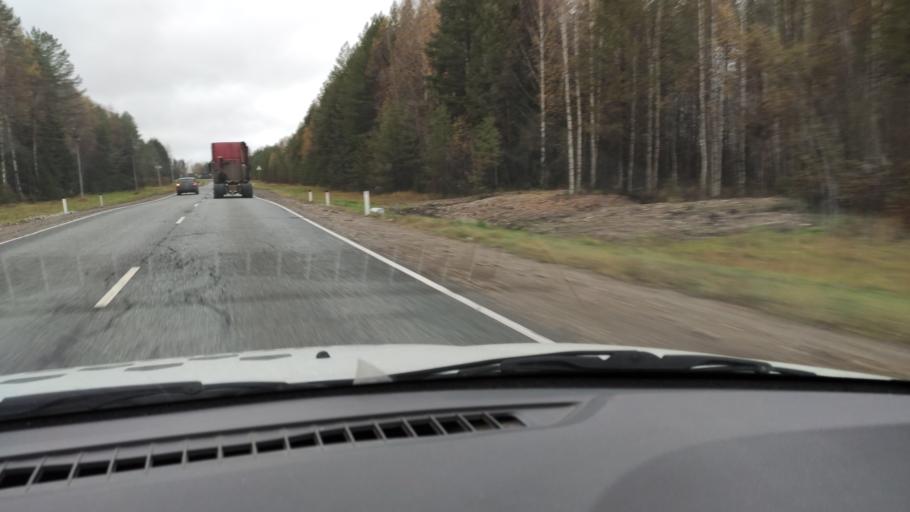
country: RU
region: Kirov
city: Belaya Kholunitsa
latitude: 58.8523
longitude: 50.7357
